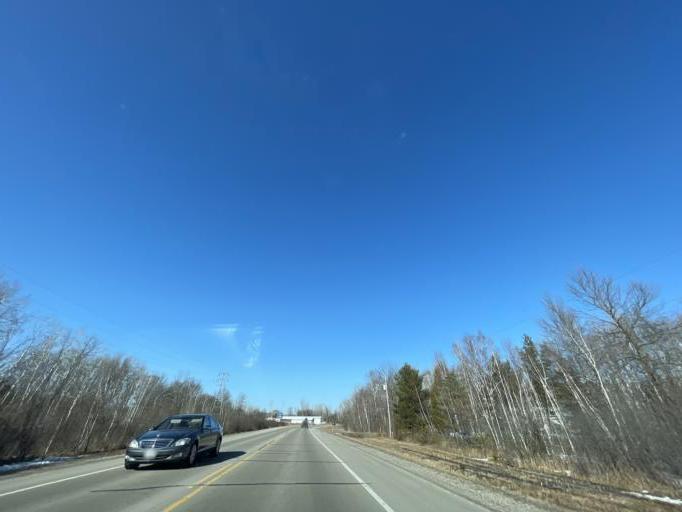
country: US
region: Wisconsin
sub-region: Brown County
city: Suamico
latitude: 44.6005
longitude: -88.0778
